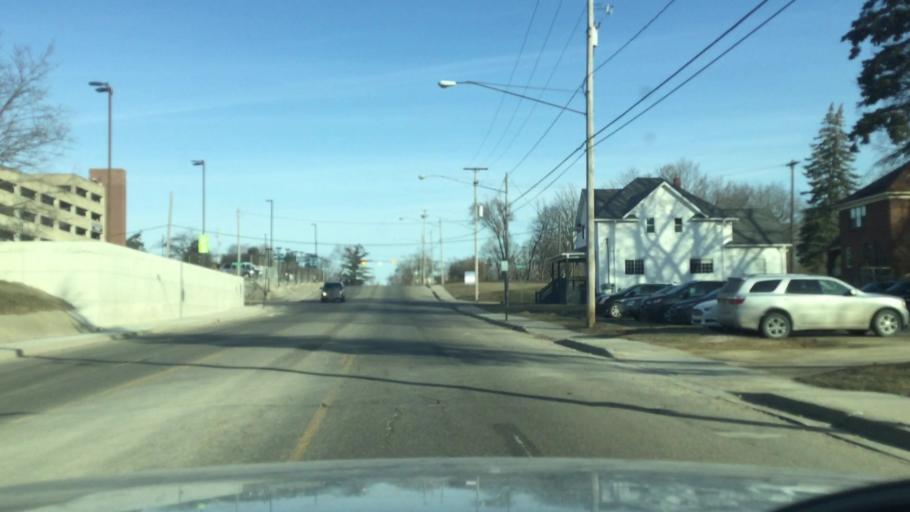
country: US
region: Michigan
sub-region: Genesee County
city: Flint
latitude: 43.0221
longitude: -83.7022
